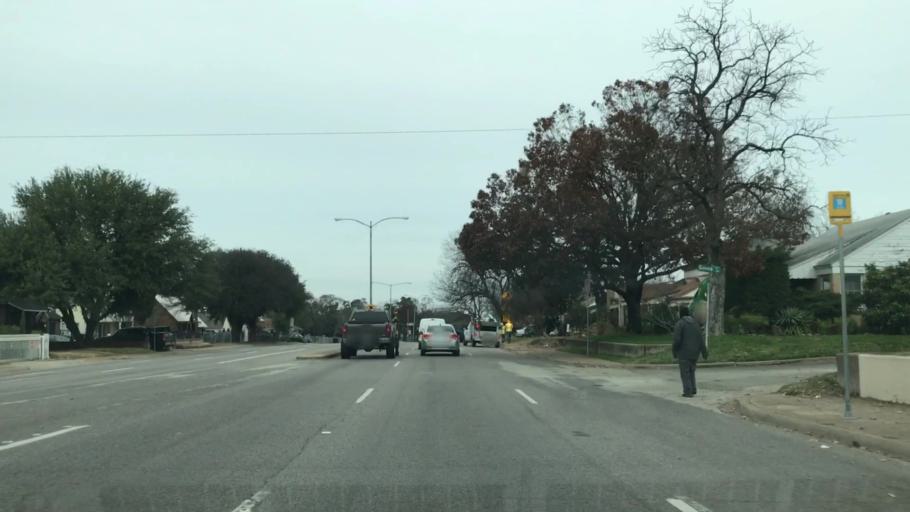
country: US
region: Texas
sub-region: Dallas County
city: Dallas
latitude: 32.7312
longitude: -96.8143
